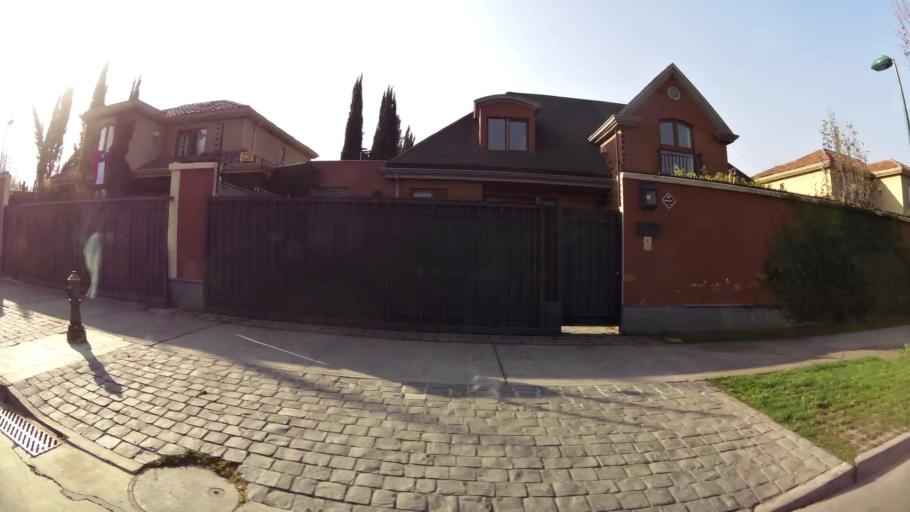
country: CL
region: Santiago Metropolitan
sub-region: Provincia de Santiago
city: Villa Presidente Frei, Nunoa, Santiago, Chile
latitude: -33.3601
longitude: -70.5359
